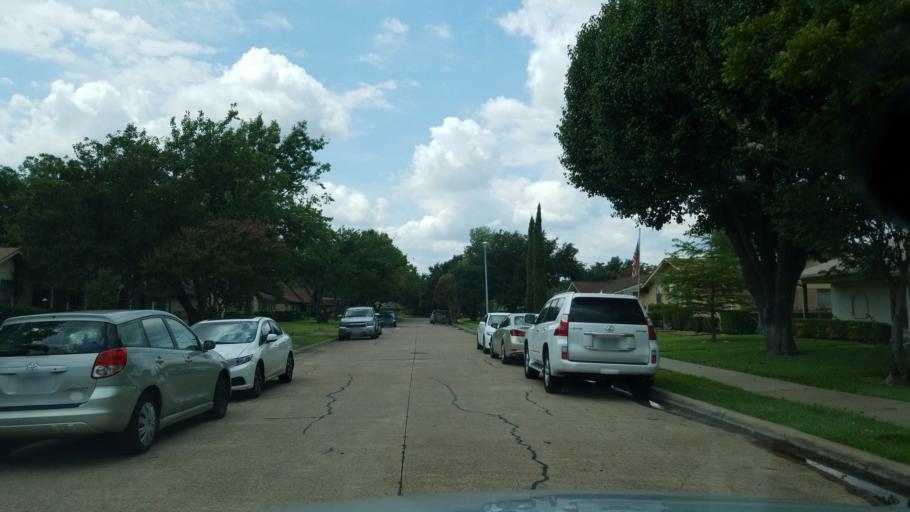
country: US
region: Texas
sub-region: Dallas County
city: Garland
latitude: 32.9276
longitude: -96.6551
